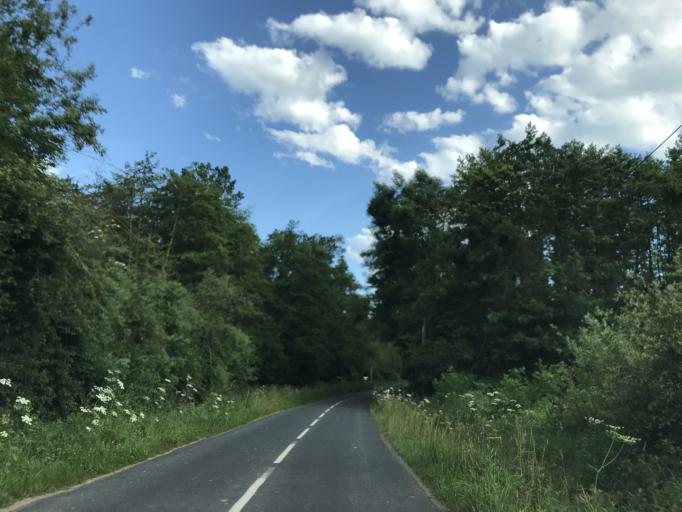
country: FR
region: Auvergne
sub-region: Departement du Puy-de-Dome
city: Courpiere
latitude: 45.7640
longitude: 3.6015
